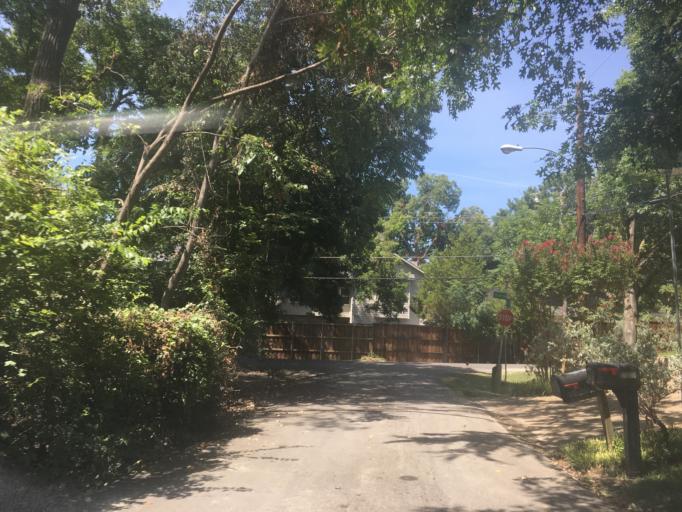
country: US
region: Texas
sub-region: Dallas County
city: Highland Park
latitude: 32.8655
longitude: -96.7259
